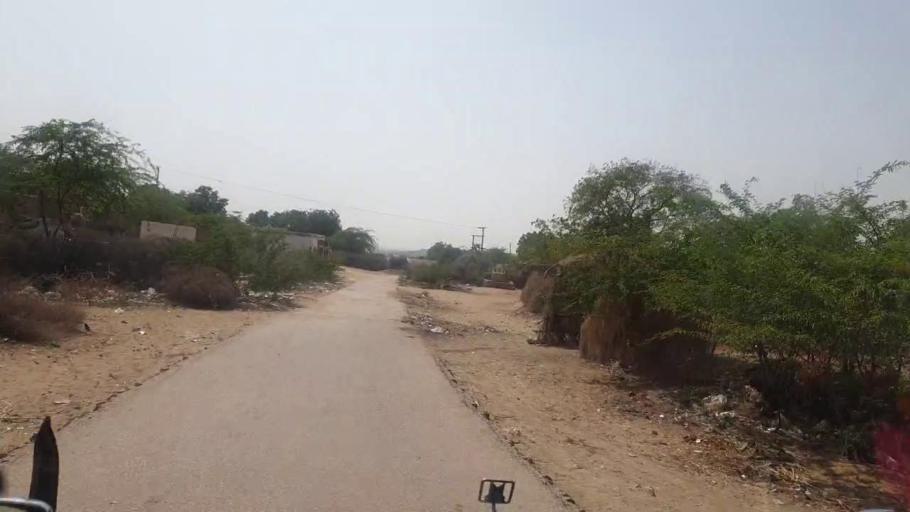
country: PK
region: Sindh
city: Islamkot
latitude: 25.1270
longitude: 70.2134
